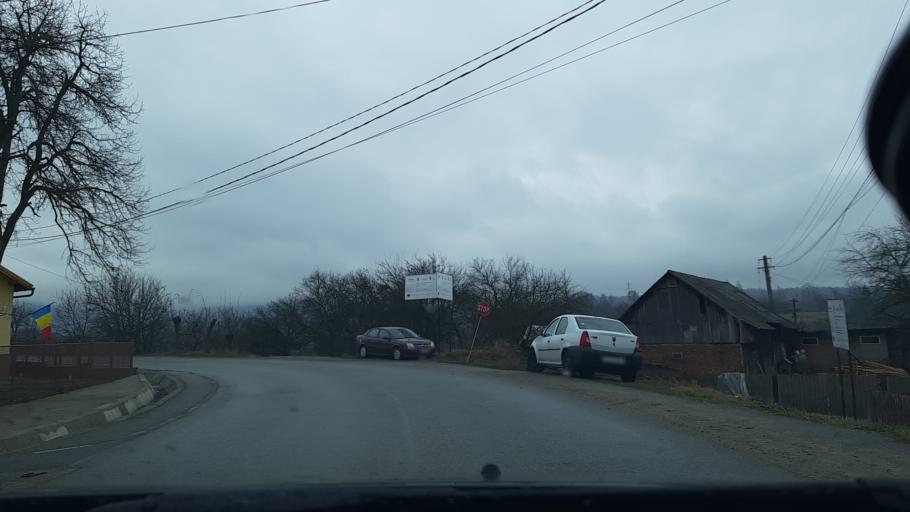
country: RO
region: Hunedoara
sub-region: Oras Petrila
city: Petrila
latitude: 45.4405
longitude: 23.4115
